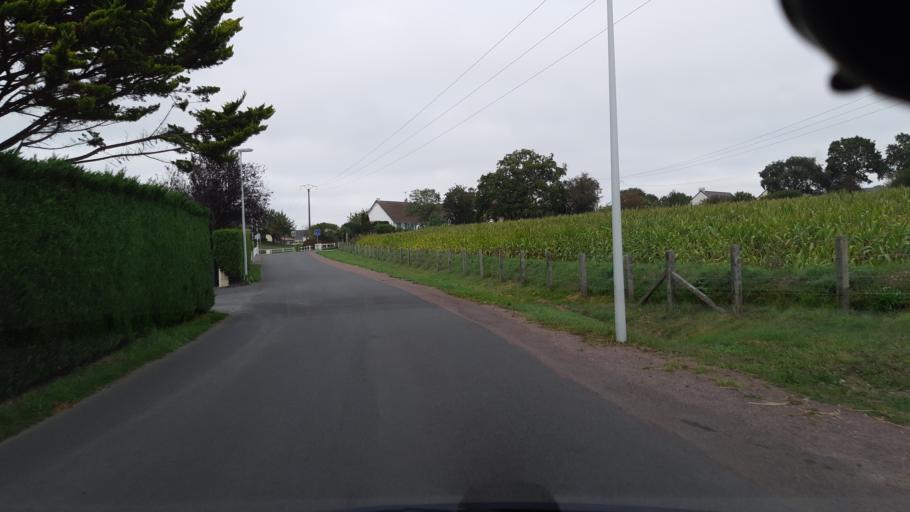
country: FR
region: Lower Normandy
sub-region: Departement de la Manche
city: Saint-Planchers
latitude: 48.8412
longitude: -1.5449
